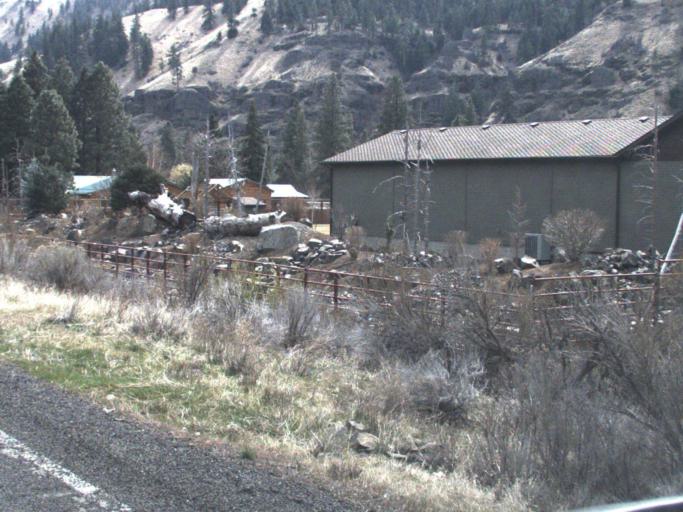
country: US
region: Washington
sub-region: Yakima County
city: Tieton
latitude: 46.7772
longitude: -120.8587
